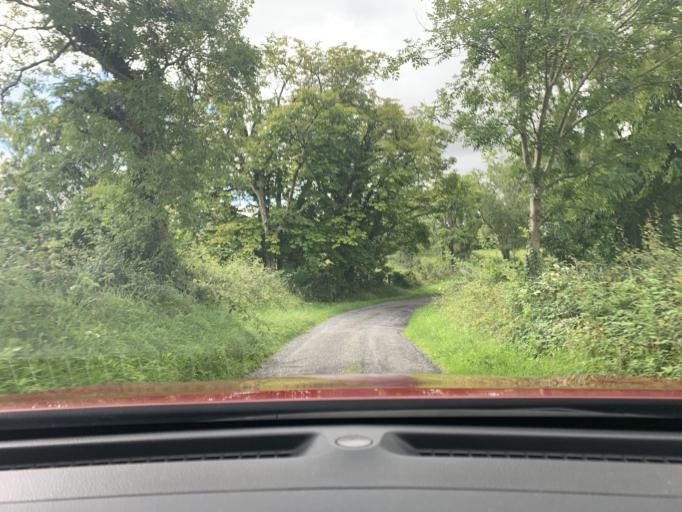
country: GB
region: Northern Ireland
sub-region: Fermanagh District
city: Enniskillen
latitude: 54.2768
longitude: -7.8061
